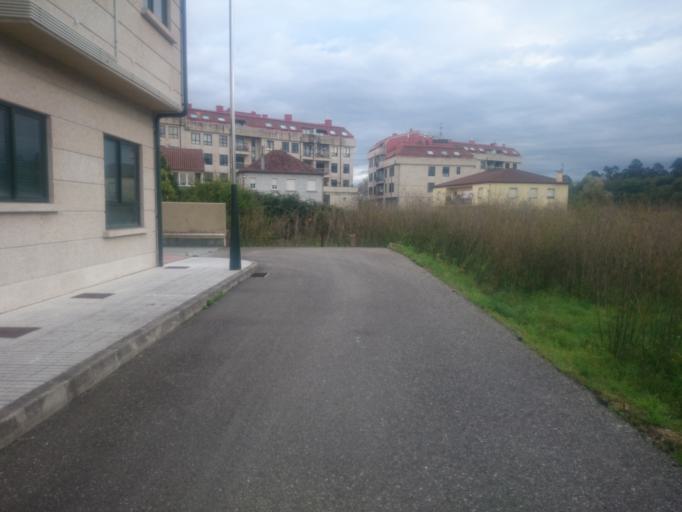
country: ES
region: Galicia
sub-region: Provincia de Pontevedra
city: Porrino
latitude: 42.1555
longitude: -8.6216
